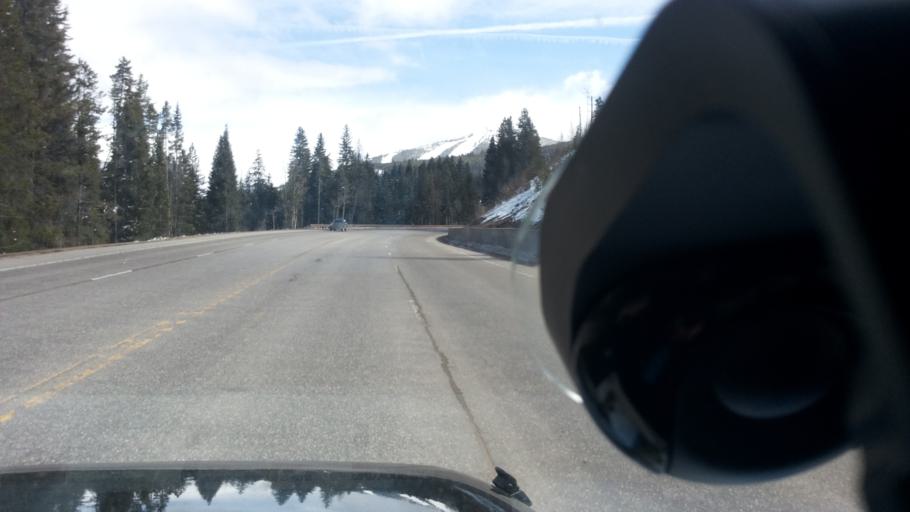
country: US
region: Colorado
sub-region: Grand County
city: Fraser
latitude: 39.9086
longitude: -105.7812
